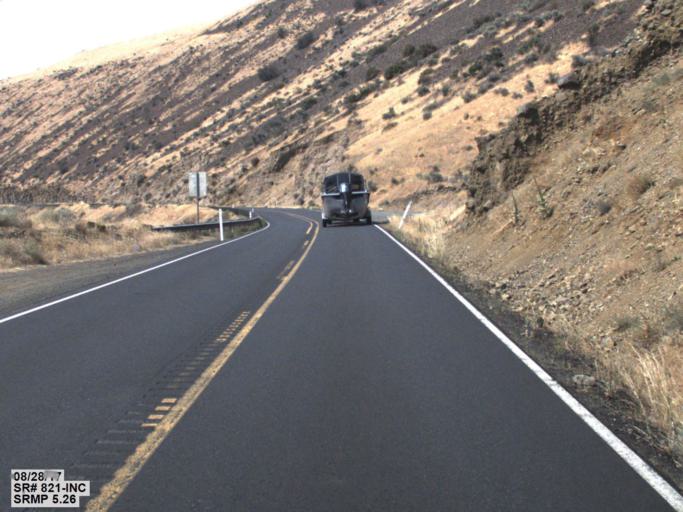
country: US
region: Washington
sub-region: Yakima County
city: Selah
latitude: 46.7434
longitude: -120.4481
